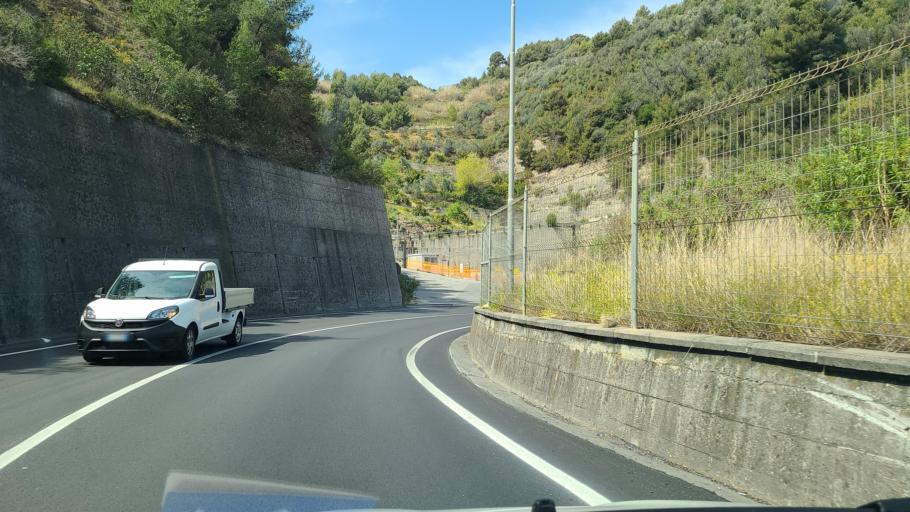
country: IT
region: Liguria
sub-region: Provincia di Imperia
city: Taggia
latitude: 43.8551
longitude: 7.8387
